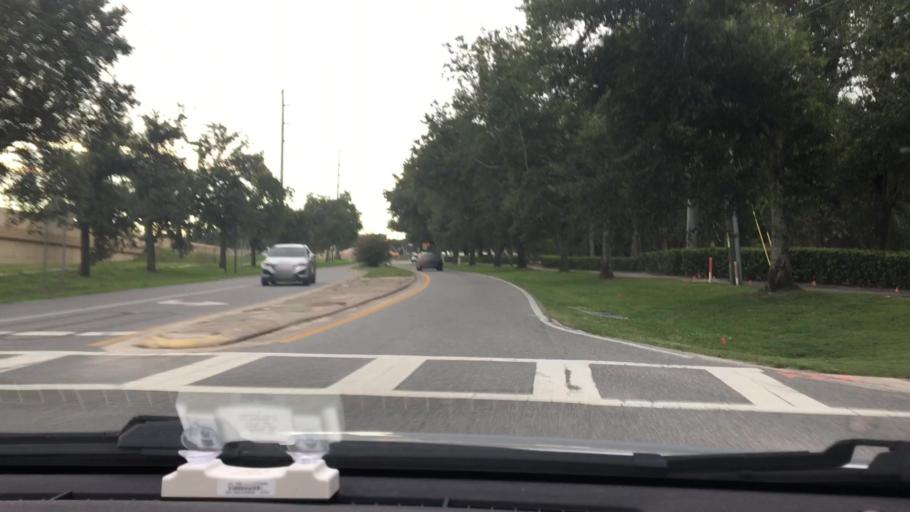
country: US
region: Florida
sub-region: Orange County
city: Eatonville
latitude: 28.6328
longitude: -81.3853
